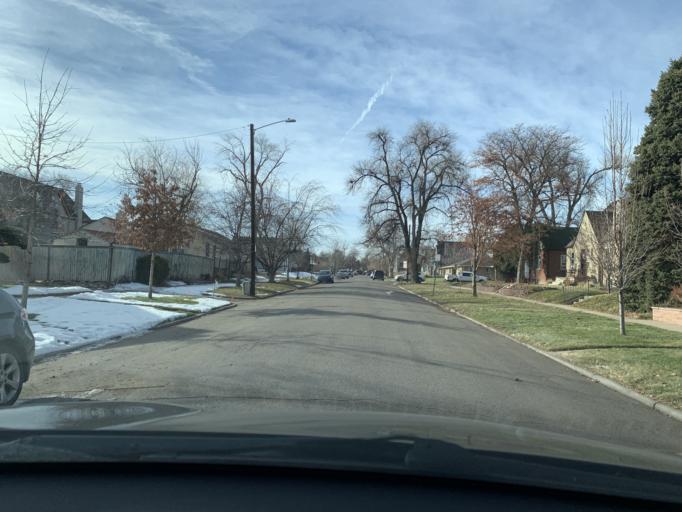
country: US
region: Colorado
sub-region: Jefferson County
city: Edgewater
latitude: 39.7525
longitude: -105.0306
